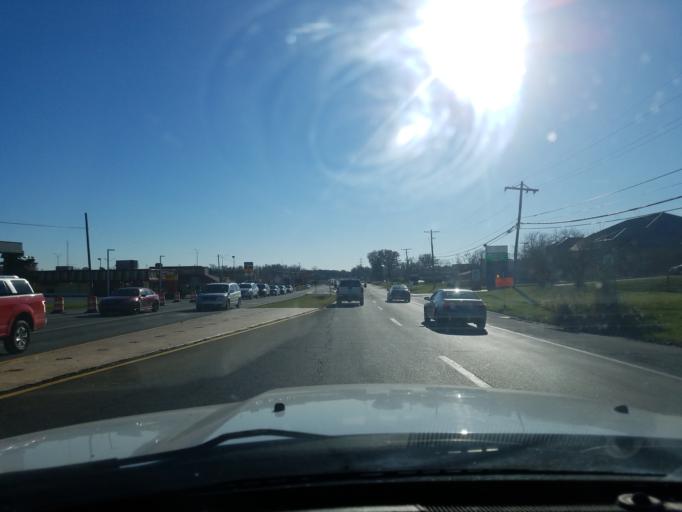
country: US
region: Indiana
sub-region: Clark County
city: Oak Park
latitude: 38.3225
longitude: -85.7132
